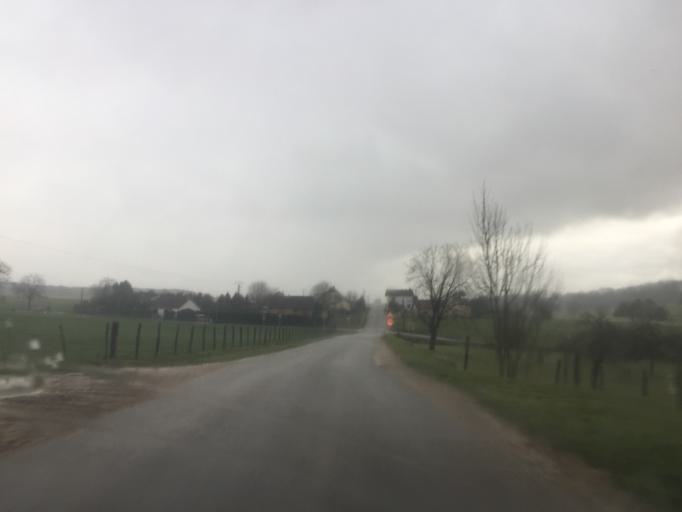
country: FR
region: Franche-Comte
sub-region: Departement du Jura
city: Dampierre
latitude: 47.2256
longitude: 5.7068
